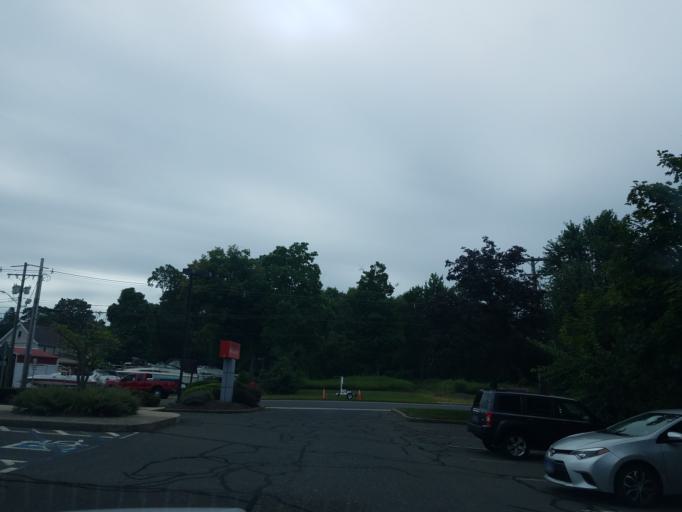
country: US
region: Connecticut
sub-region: Hartford County
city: Plainville
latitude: 41.6730
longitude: -72.8638
